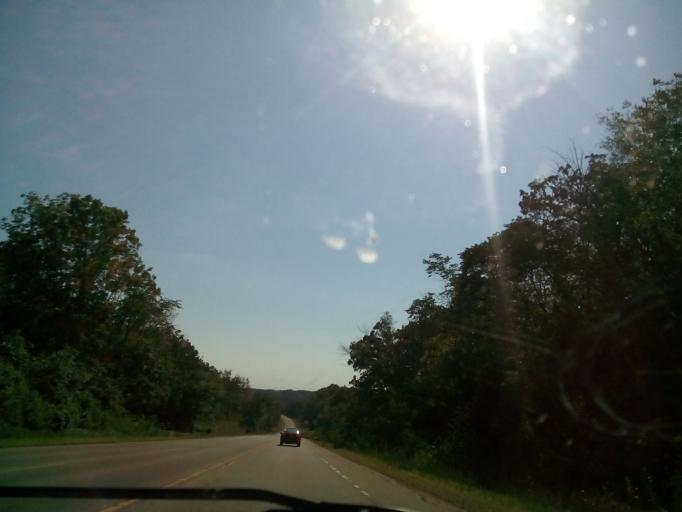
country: US
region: Wisconsin
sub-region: Green County
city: New Glarus
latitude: 42.8643
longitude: -89.6085
